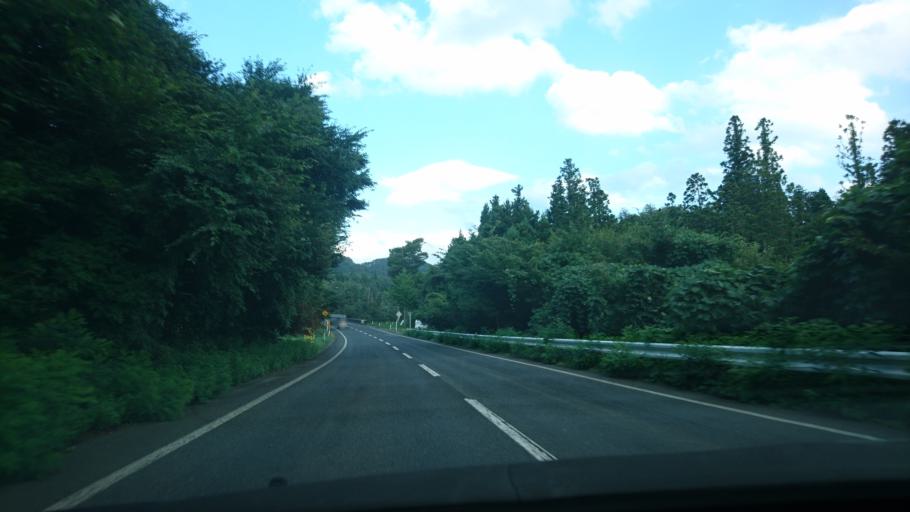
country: JP
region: Iwate
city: Mizusawa
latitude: 39.0358
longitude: 141.2525
